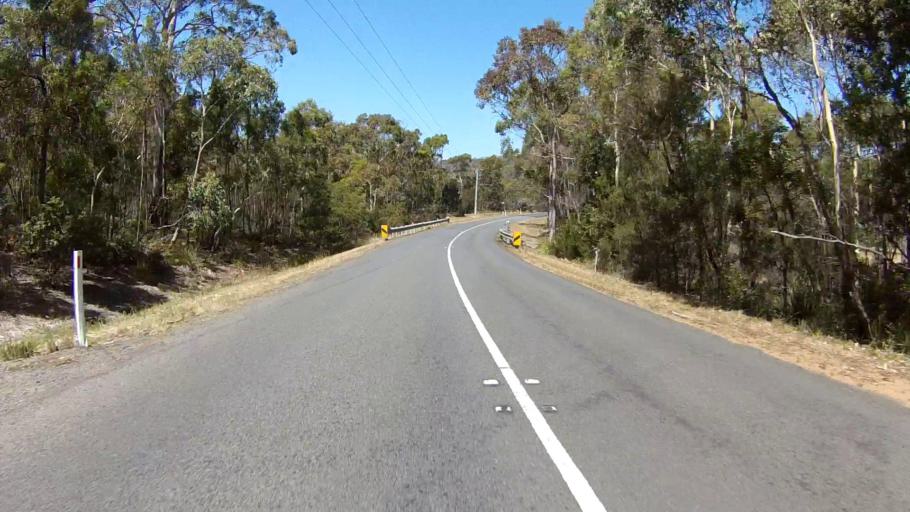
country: AU
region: Tasmania
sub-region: Clarence
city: Sandford
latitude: -42.9781
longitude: 147.4827
